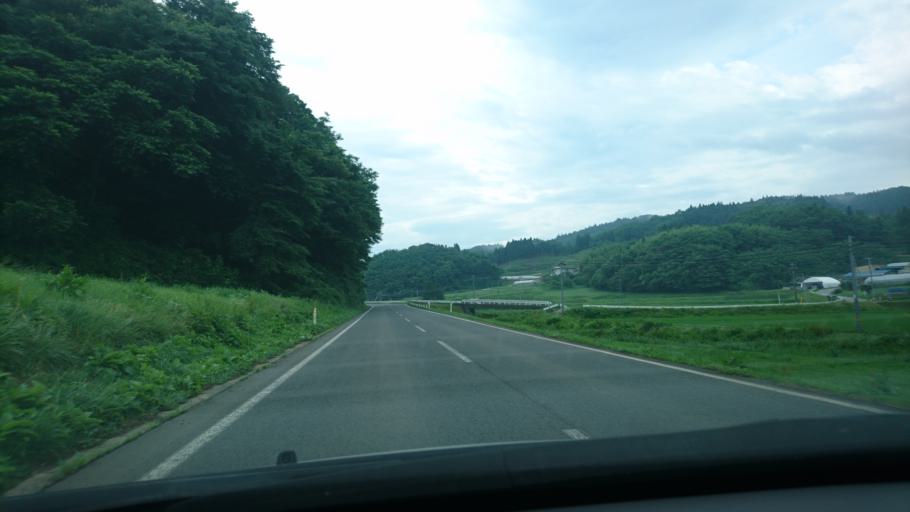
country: JP
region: Iwate
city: Ichinoseki
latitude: 38.9200
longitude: 141.4203
